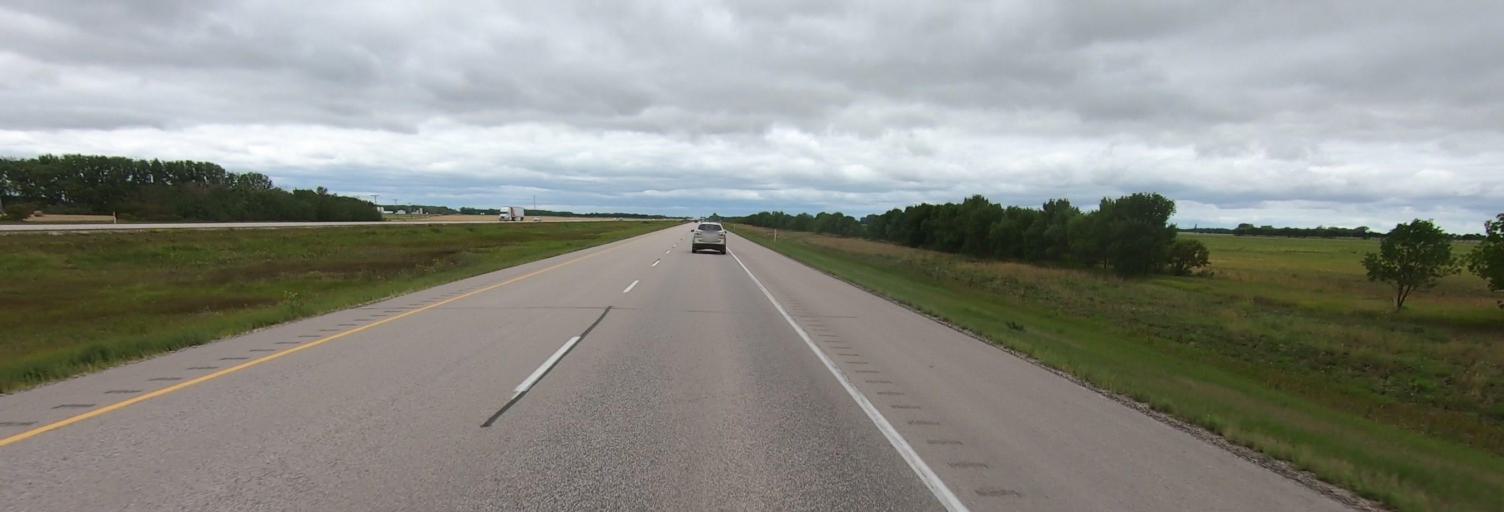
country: CA
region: Manitoba
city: Portage la Prairie
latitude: 49.9459
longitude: -97.9665
